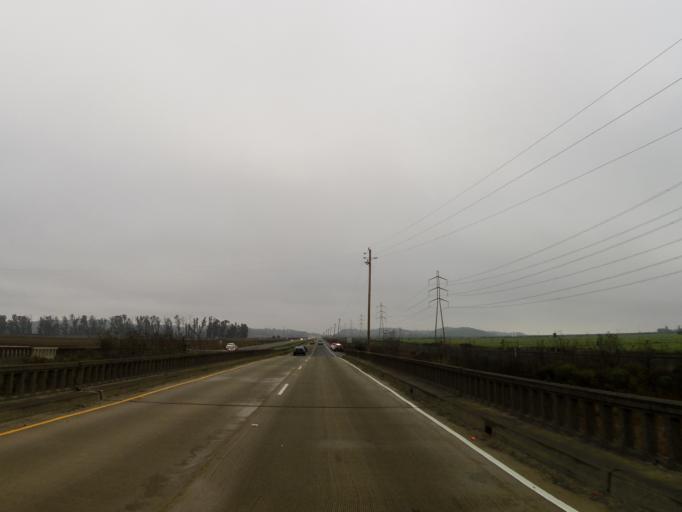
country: US
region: California
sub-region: Marin County
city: Black Point-Green Point
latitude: 38.0875
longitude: -122.5341
